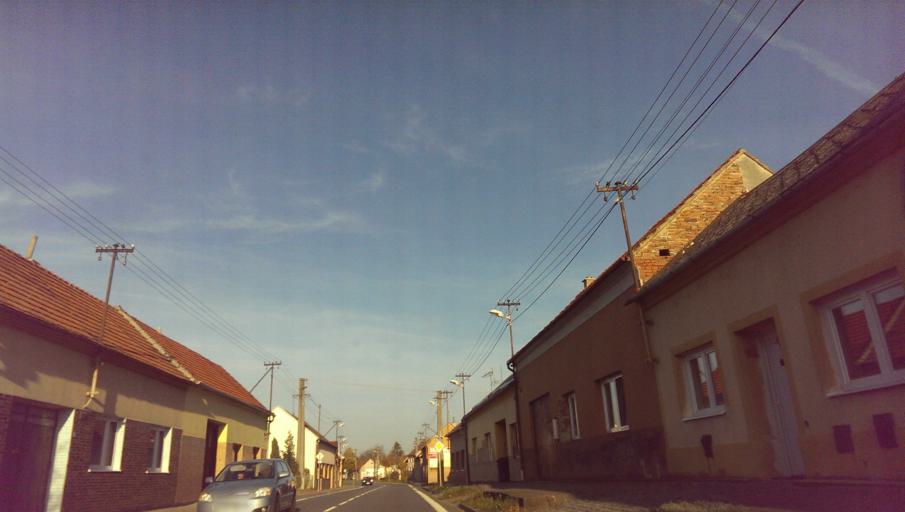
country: CZ
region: Zlin
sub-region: Okres Zlin
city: Ostrozska Nova Ves
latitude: 48.9962
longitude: 17.4272
